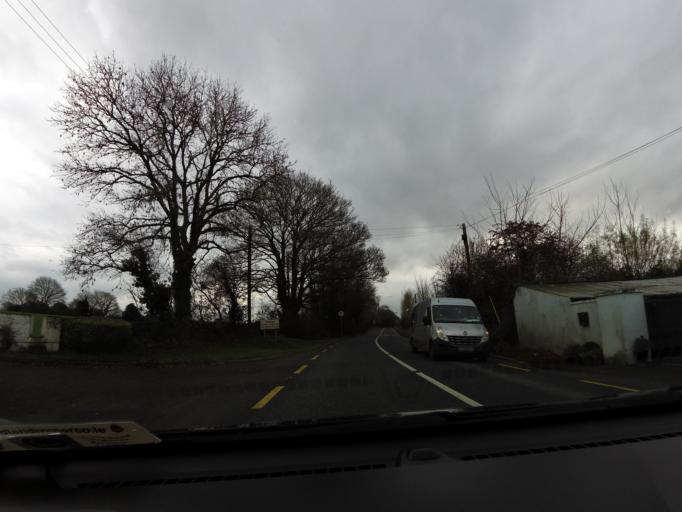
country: IE
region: Leinster
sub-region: Kilkenny
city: Kilkenny
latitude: 52.6891
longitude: -7.2572
